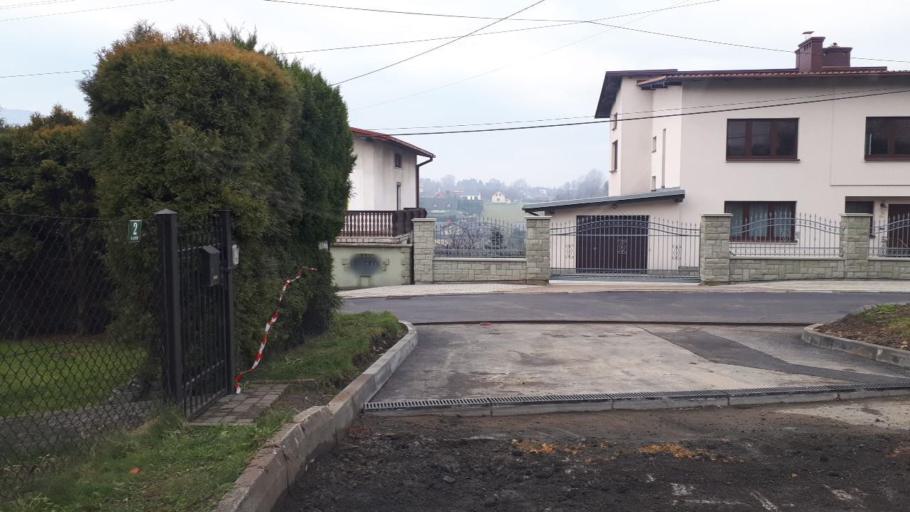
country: PL
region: Silesian Voivodeship
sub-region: Powiat bielski
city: Kozy
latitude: 49.8435
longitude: 19.1469
